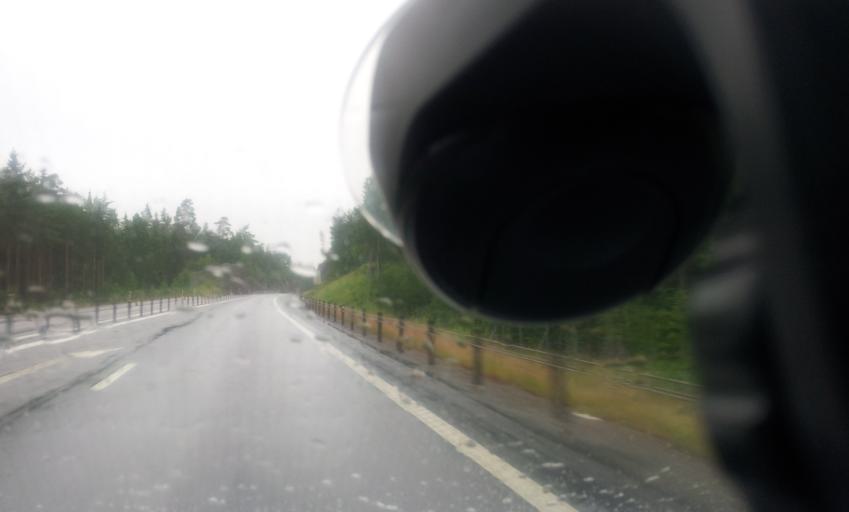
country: SE
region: OEstergoetland
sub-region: Valdemarsviks Kommun
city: Gusum
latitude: 58.3454
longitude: 16.4486
